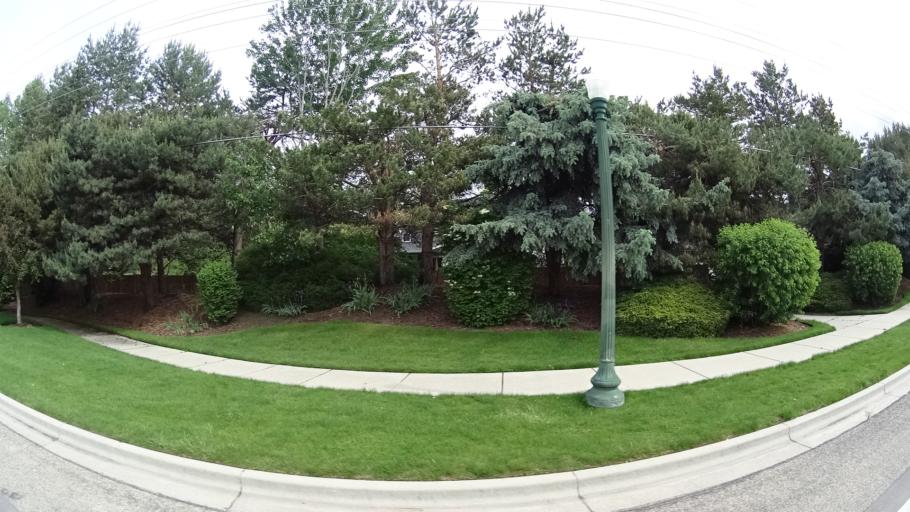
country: US
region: Idaho
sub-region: Ada County
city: Eagle
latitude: 43.6957
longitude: -116.3718
